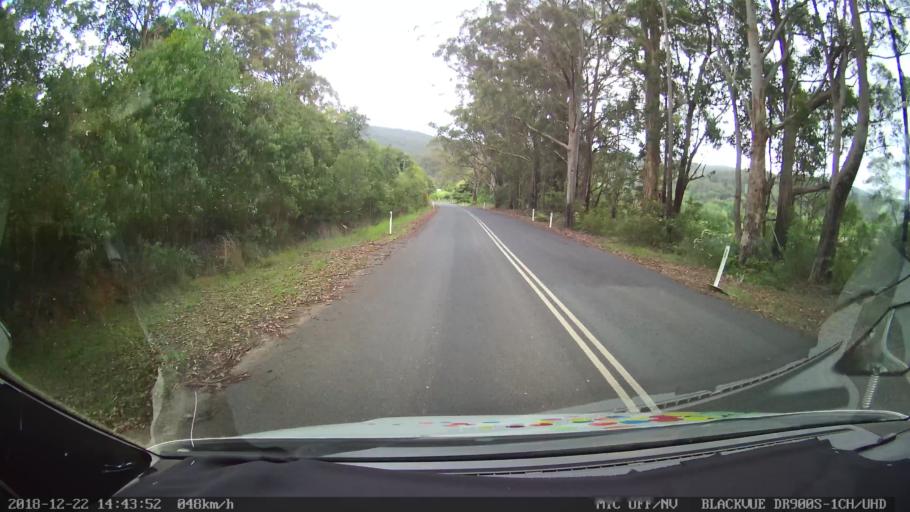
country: AU
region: New South Wales
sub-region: Bellingen
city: Dorrigo
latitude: -30.1644
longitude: 152.5810
